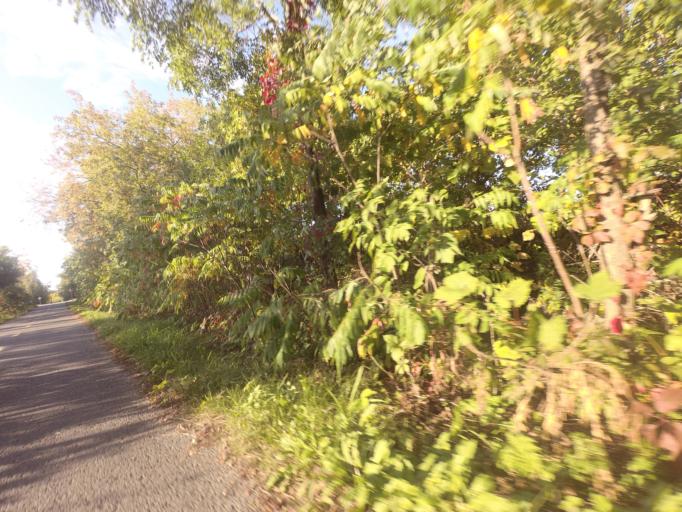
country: CA
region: Quebec
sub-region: Laurentides
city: Saint-Jerome
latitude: 45.8038
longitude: -74.0086
